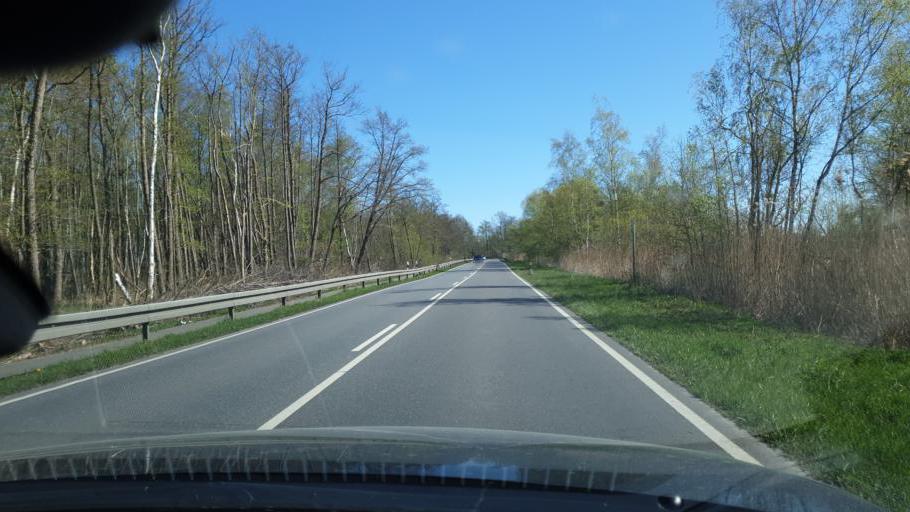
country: DE
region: Mecklenburg-Vorpommern
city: Werdervorstadt
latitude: 53.6603
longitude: 11.4459
